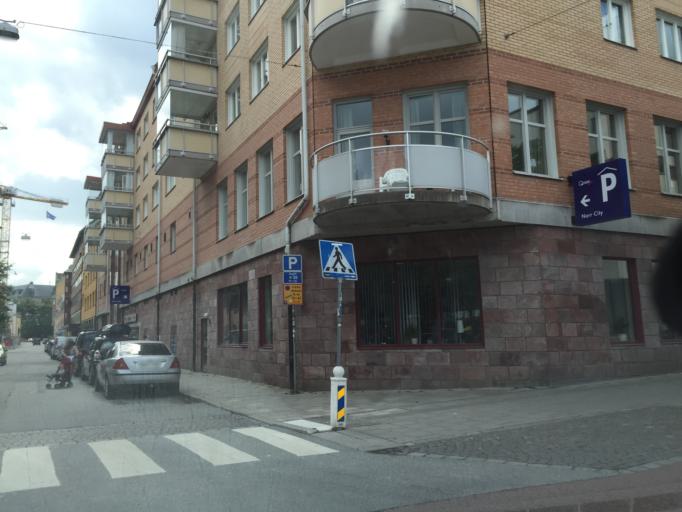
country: SE
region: OErebro
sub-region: Orebro Kommun
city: Orebro
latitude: 59.2773
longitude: 15.2180
